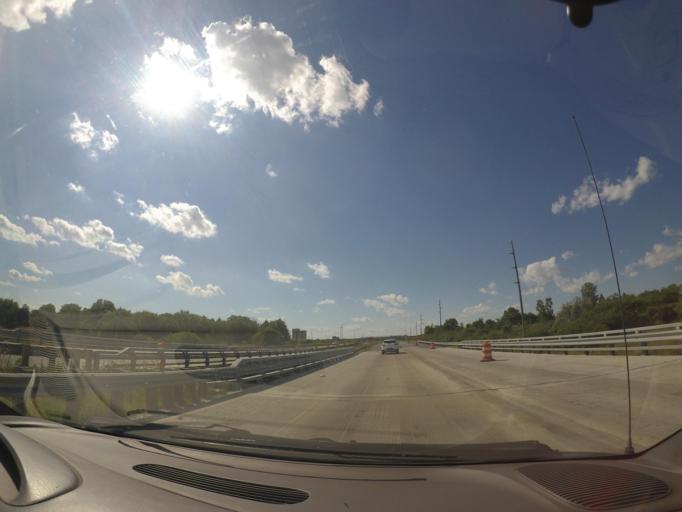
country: US
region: Ohio
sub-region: Sandusky County
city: Fremont
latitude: 41.3602
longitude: -83.0821
